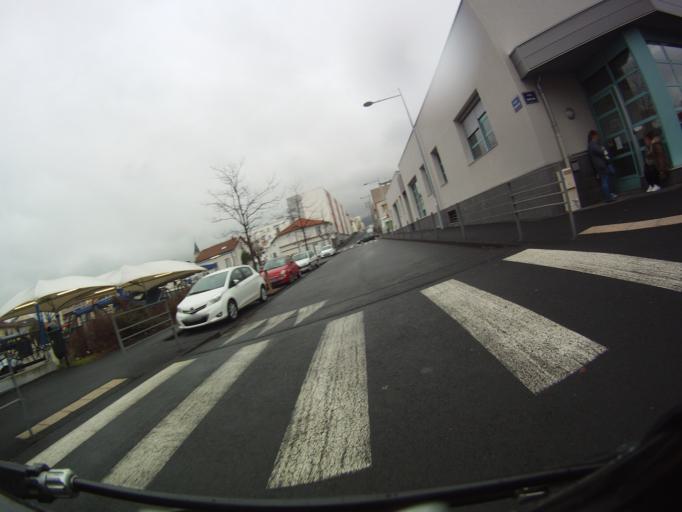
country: FR
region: Auvergne
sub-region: Departement du Puy-de-Dome
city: Clermont-Ferrand
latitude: 45.7652
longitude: 3.0978
